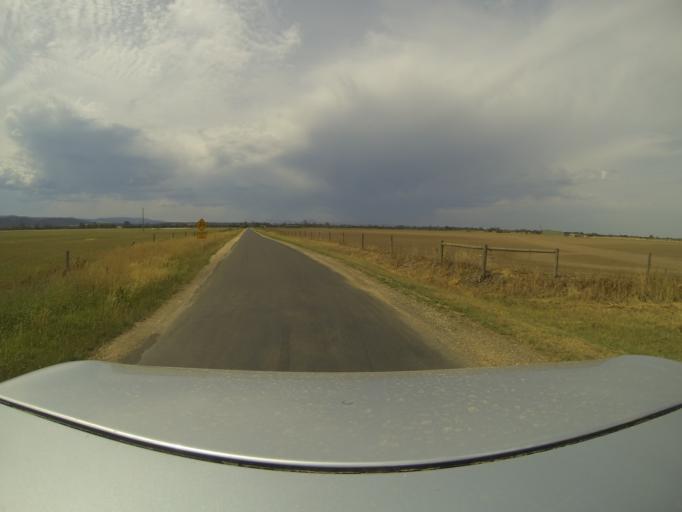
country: AU
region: Victoria
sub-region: Wellington
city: Heyfield
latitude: -37.9987
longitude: 146.6915
